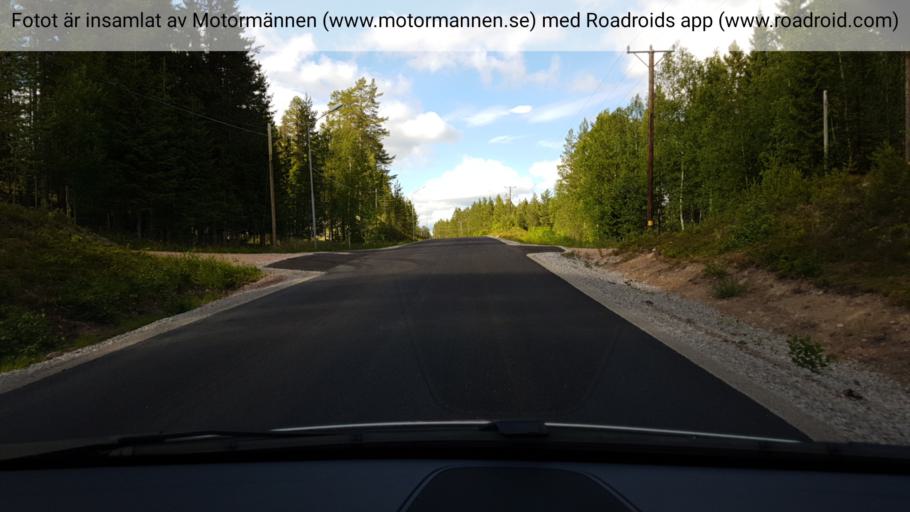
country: SE
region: Jaemtland
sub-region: Harjedalens Kommun
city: Sveg
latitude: 61.8135
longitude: 14.1105
